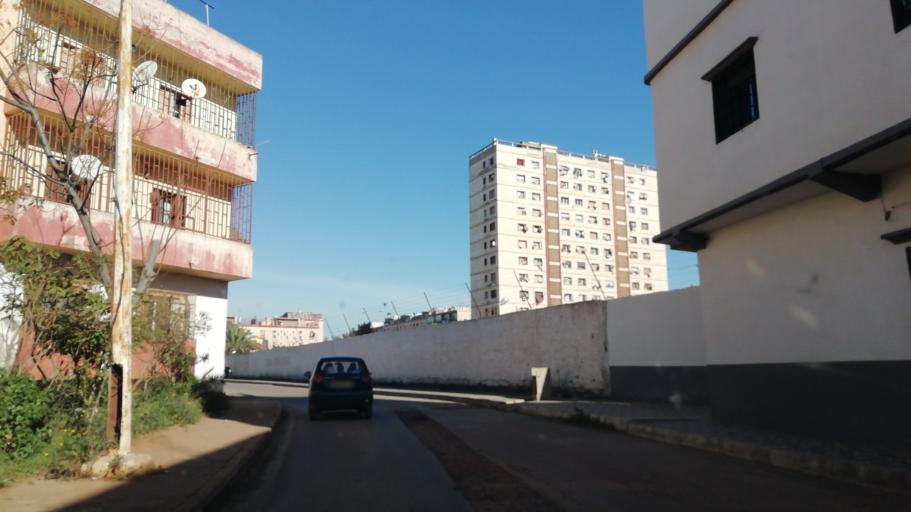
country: DZ
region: Oran
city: Oran
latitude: 35.6770
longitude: -0.6455
